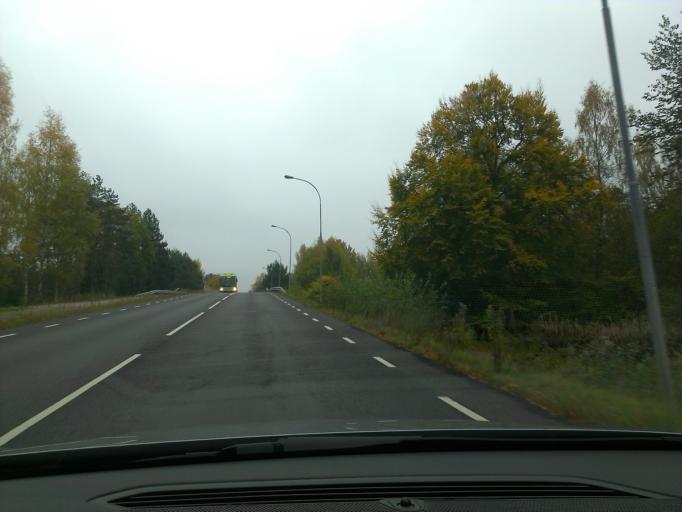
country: SE
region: Kronoberg
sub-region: Vaxjo Kommun
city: Vaexjoe
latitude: 56.8881
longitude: 14.7474
